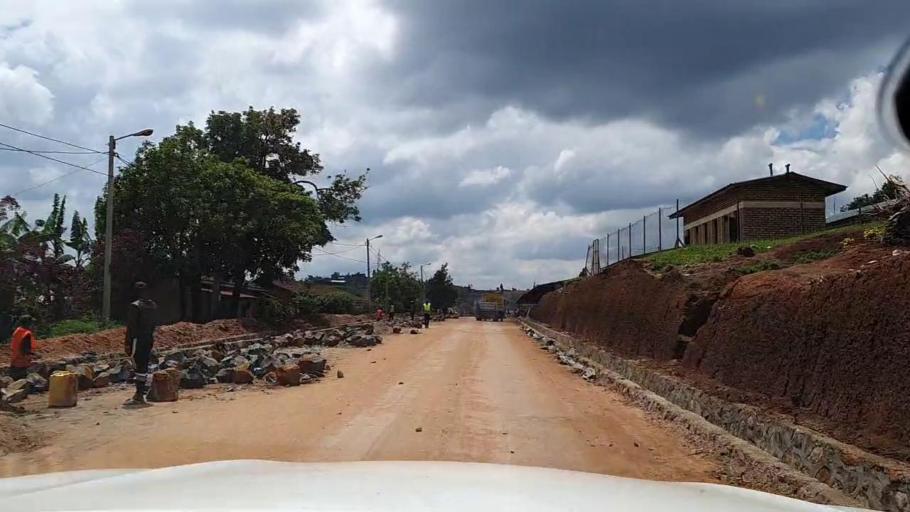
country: RW
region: Southern Province
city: Butare
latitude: -2.6942
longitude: 29.5691
